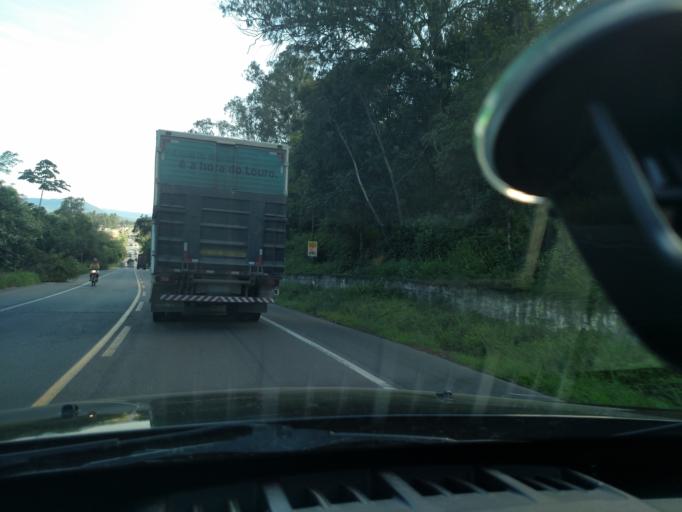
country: BR
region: Santa Catarina
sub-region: Ibirama
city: Ibirama
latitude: -27.1151
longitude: -49.5318
